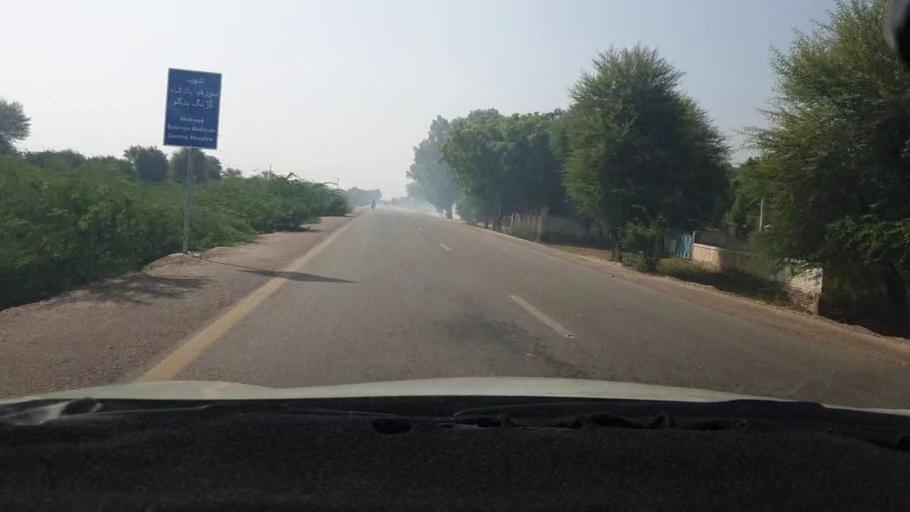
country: PK
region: Sindh
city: Sanghar
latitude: 25.9958
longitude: 68.9639
